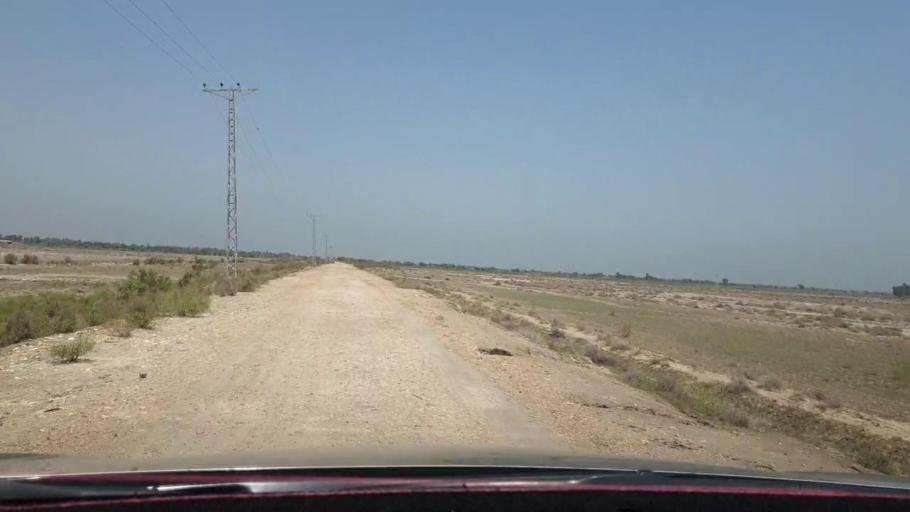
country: PK
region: Sindh
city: Warah
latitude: 27.3927
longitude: 67.6844
